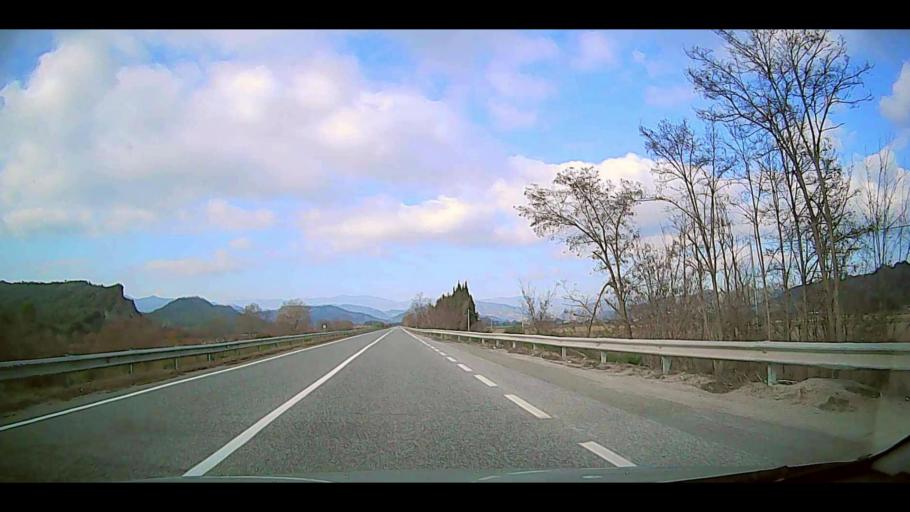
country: IT
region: Calabria
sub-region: Provincia di Crotone
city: Rocca di Neto
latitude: 39.1695
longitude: 16.9813
